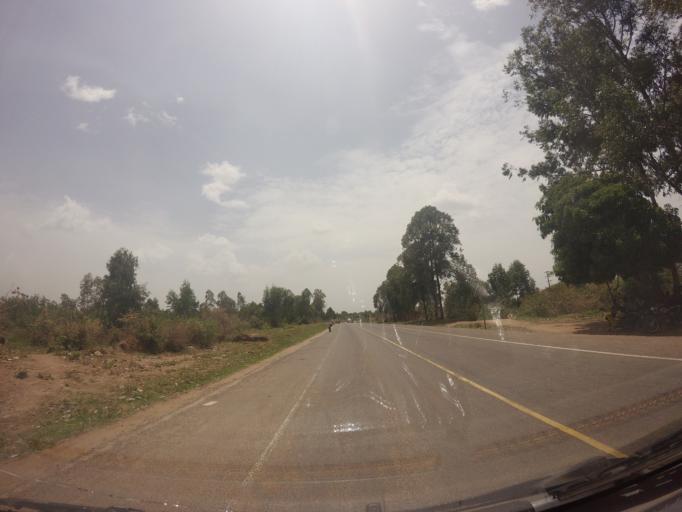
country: UG
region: Northern Region
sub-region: Arua District
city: Arua
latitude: 2.9553
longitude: 30.9155
